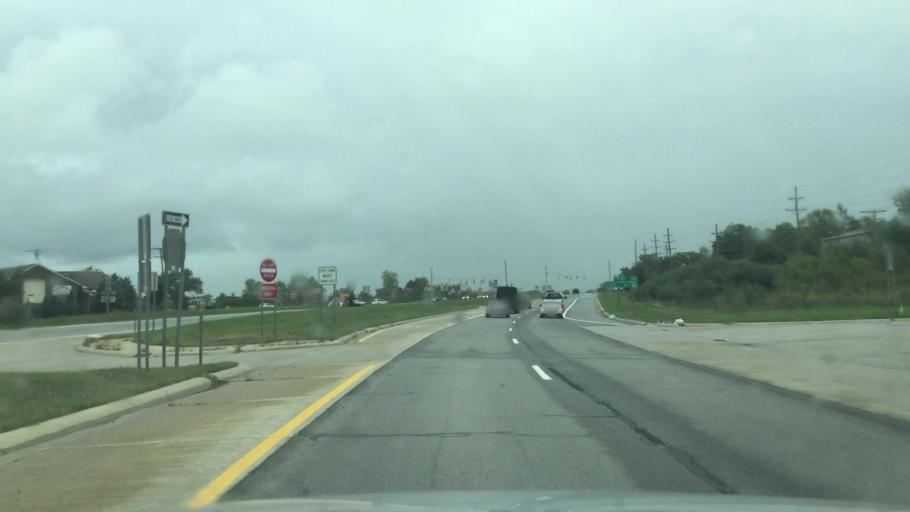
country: US
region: Michigan
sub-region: Livingston County
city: Howell
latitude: 42.6225
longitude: -83.9809
